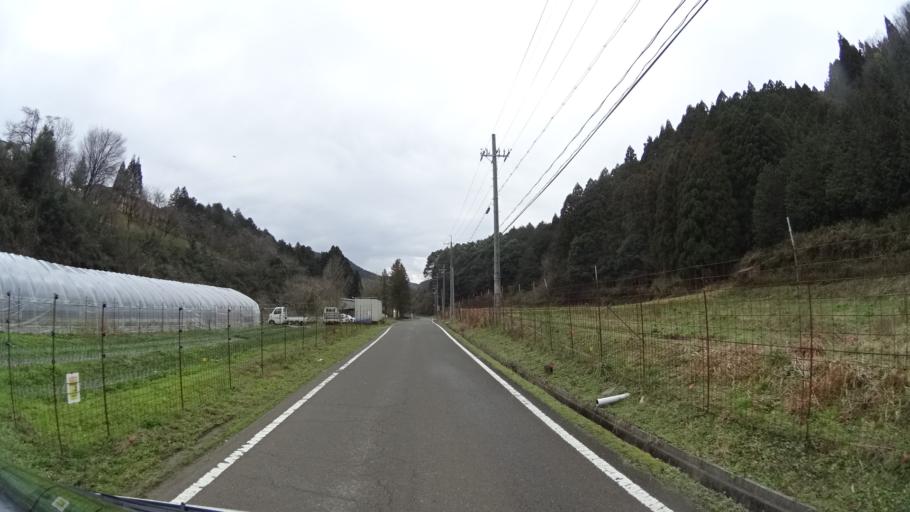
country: JP
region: Kyoto
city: Ayabe
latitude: 35.3391
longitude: 135.3479
